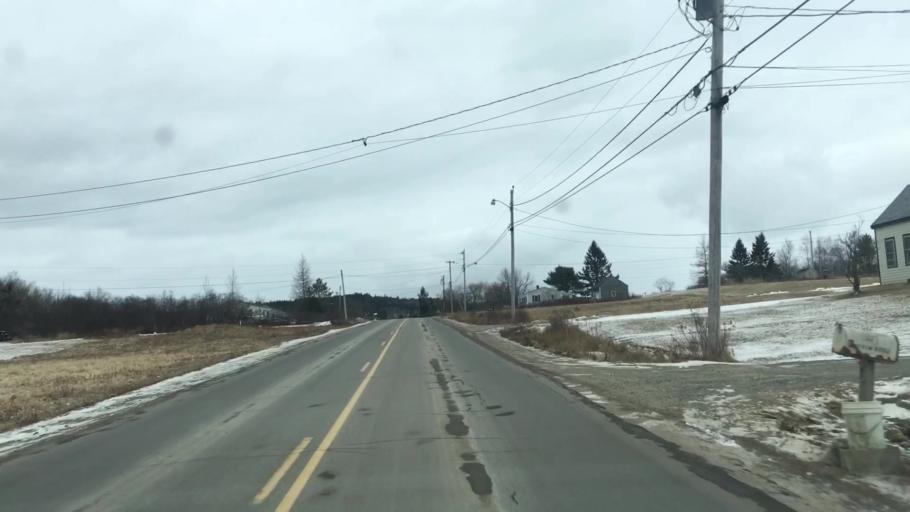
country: US
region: Maine
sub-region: Washington County
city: Machiasport
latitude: 44.7106
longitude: -67.4029
